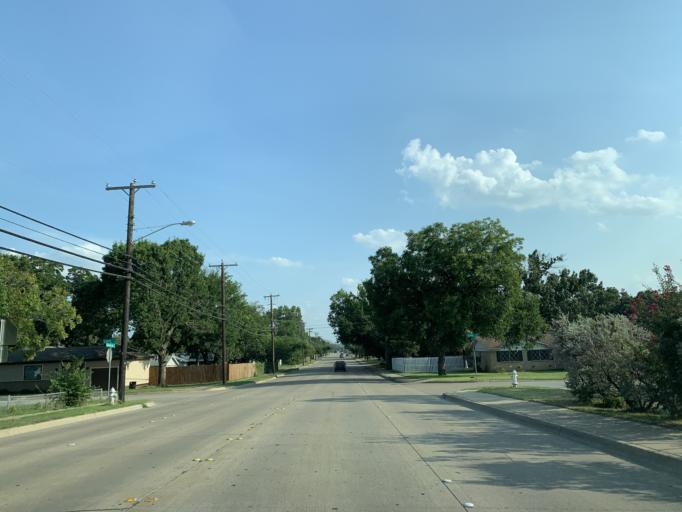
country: US
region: Texas
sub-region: Tarrant County
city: Hurst
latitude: 32.8155
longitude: -97.1866
